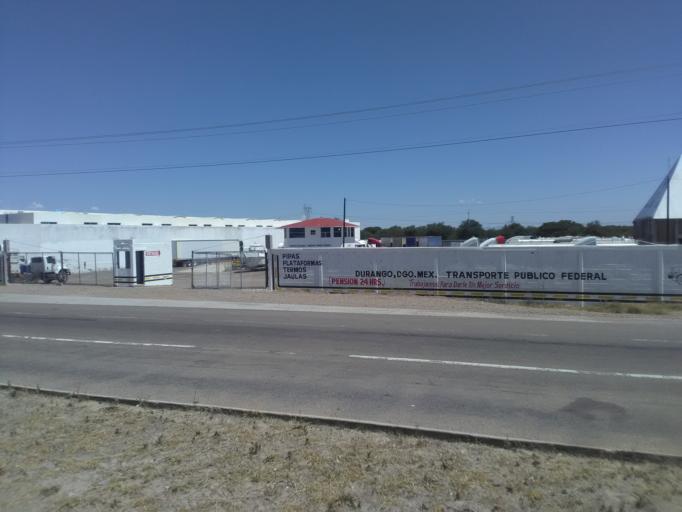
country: MX
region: Durango
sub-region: Durango
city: Jose Refugio Salcido
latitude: 24.0227
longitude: -104.5396
